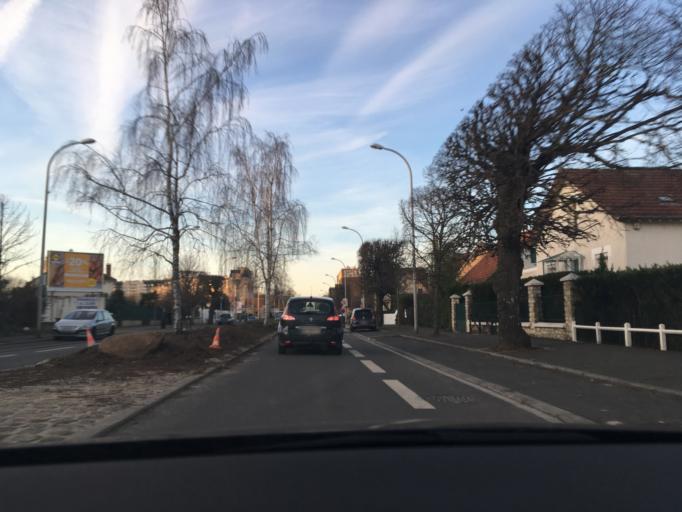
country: FR
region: Ile-de-France
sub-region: Departement de Seine-et-Marne
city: Melun
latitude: 48.5486
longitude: 2.6510
